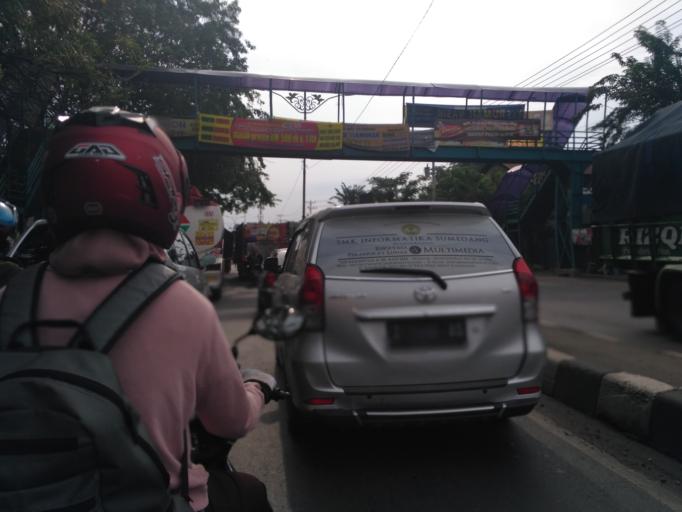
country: ID
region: Central Java
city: Semarang
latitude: -6.9841
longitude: 110.3561
